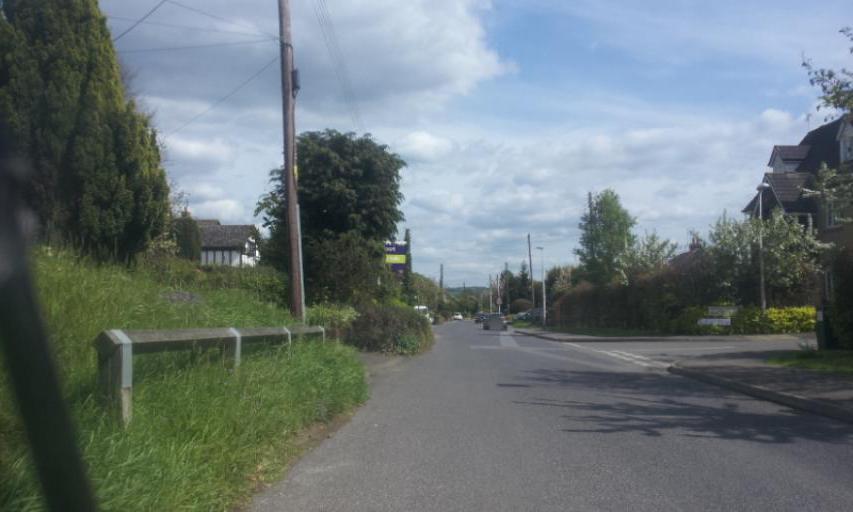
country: GB
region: England
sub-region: Medway
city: Cuxton
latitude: 51.3775
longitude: 0.4452
